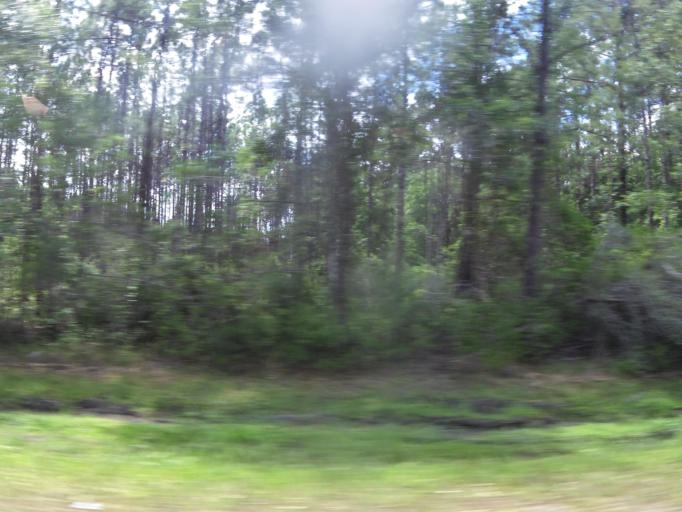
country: US
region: Florida
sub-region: Clay County
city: Green Cove Springs
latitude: 29.9377
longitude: -81.7483
